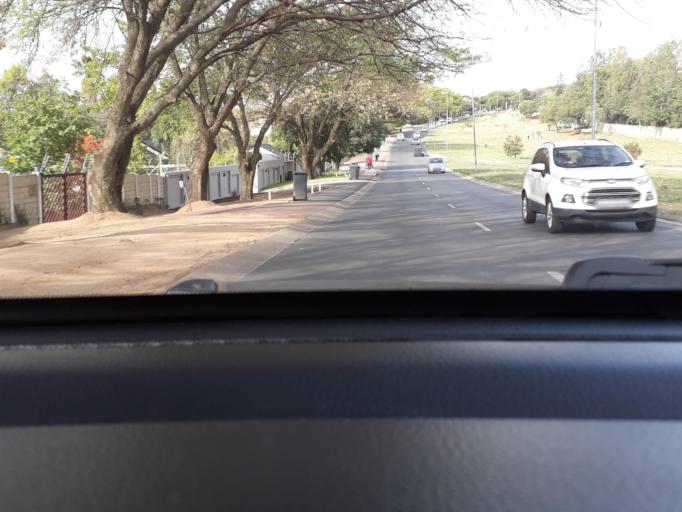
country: ZA
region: Gauteng
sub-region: City of Johannesburg Metropolitan Municipality
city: Diepsloot
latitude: -26.0353
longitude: 28.0014
